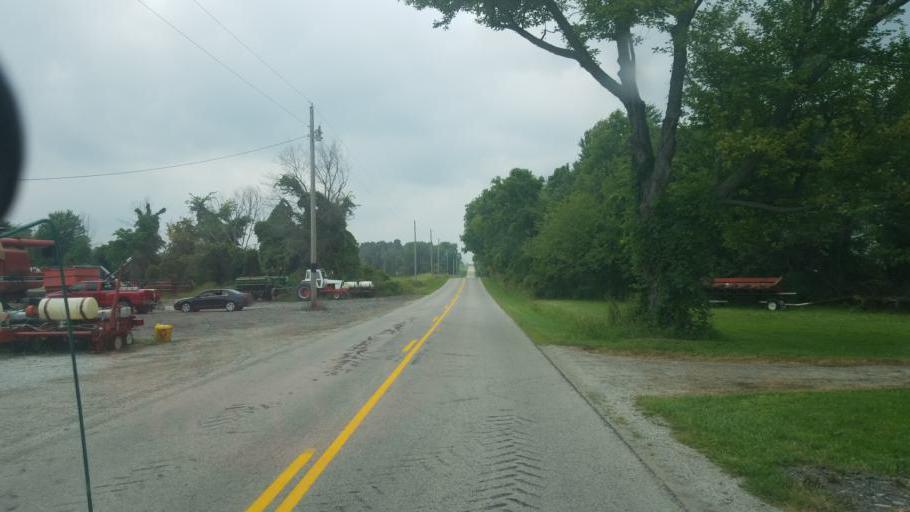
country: US
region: Ohio
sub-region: Huron County
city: Greenwich
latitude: 41.0836
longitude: -82.5656
